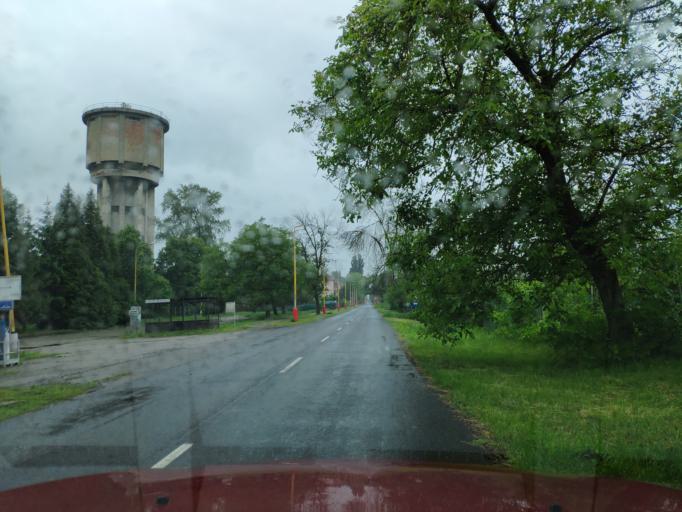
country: SK
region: Kosicky
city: Cierna nad Tisou
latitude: 48.4210
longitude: 22.0961
